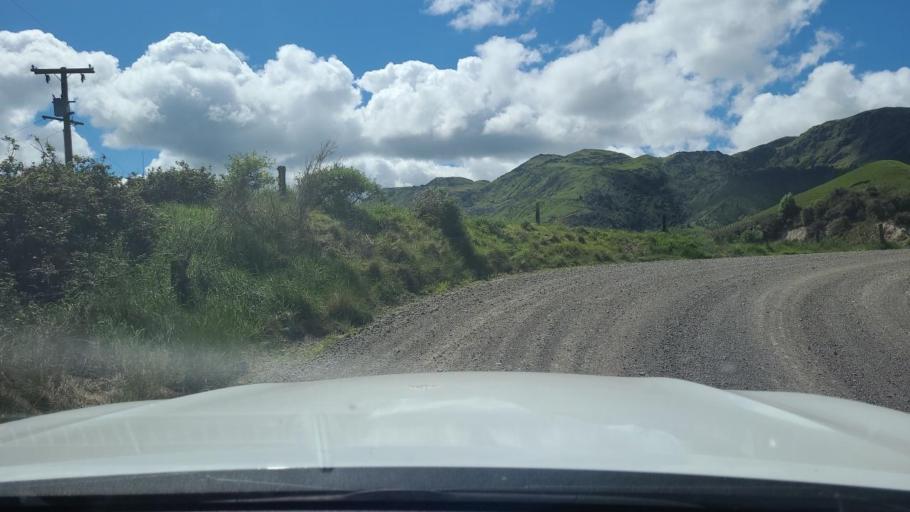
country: NZ
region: Hawke's Bay
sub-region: Napier City
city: Napier
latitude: -39.1645
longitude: 176.6734
